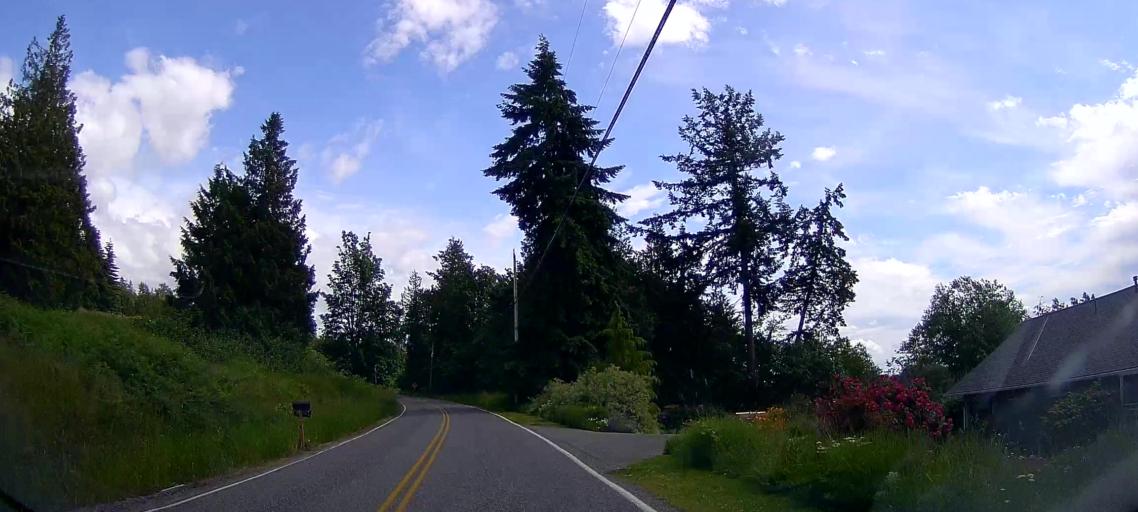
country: US
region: Washington
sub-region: Skagit County
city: Burlington
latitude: 48.5746
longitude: -122.3990
